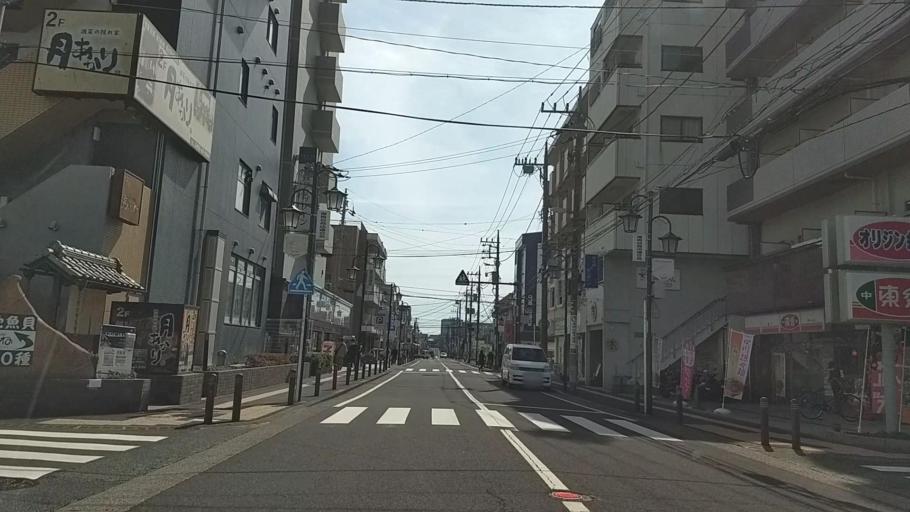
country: JP
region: Kanagawa
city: Fujisawa
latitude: 35.3956
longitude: 139.4653
